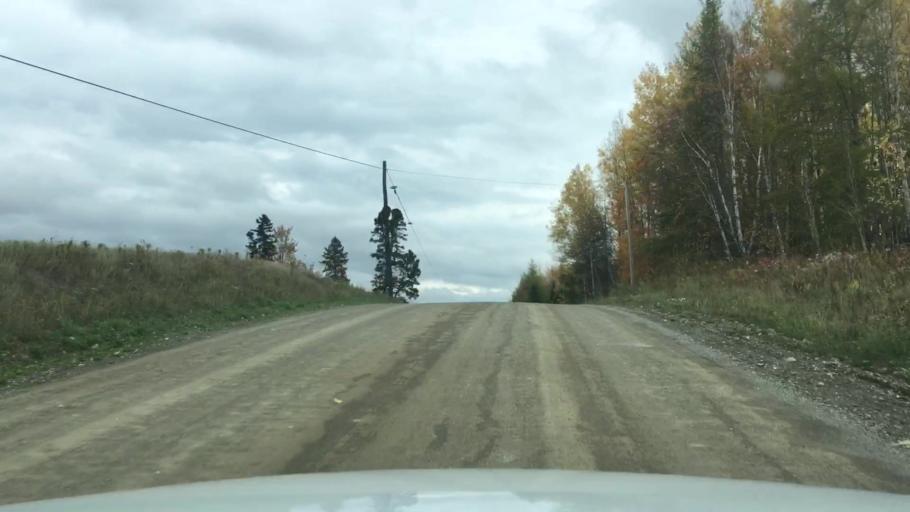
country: US
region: Maine
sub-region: Aroostook County
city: Easton
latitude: 46.5169
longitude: -67.8841
